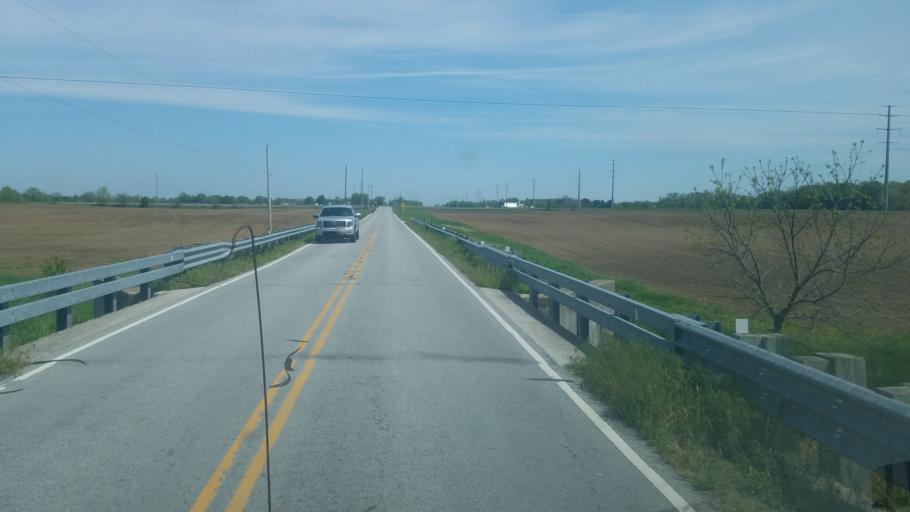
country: US
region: Ohio
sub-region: Seneca County
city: Tiffin
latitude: 41.1121
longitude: -83.1311
